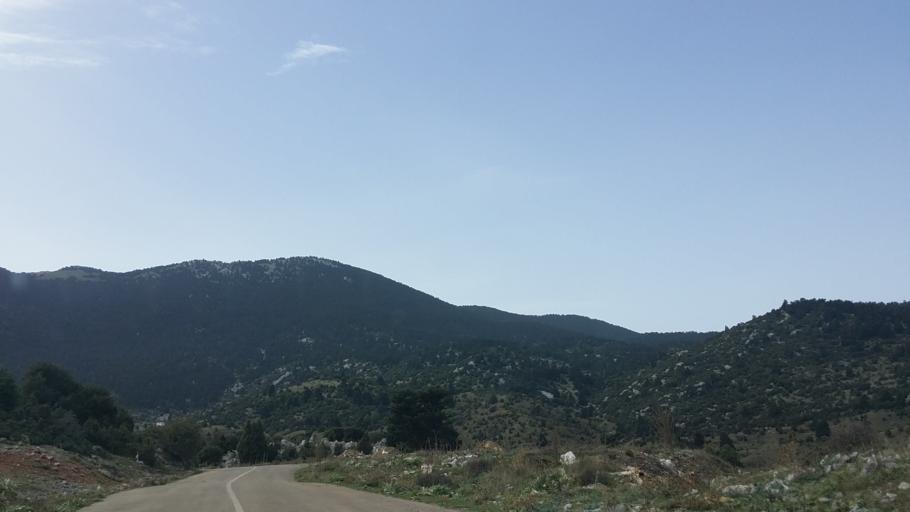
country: GR
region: Central Greece
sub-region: Nomos Voiotias
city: Livadeia
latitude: 38.3749
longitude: 22.8466
